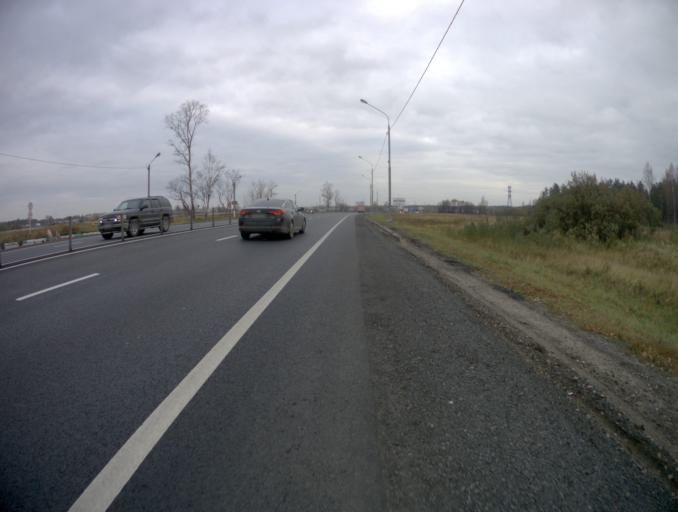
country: RU
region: Moskovskaya
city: Malaya Dubna
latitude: 55.8711
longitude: 38.9634
